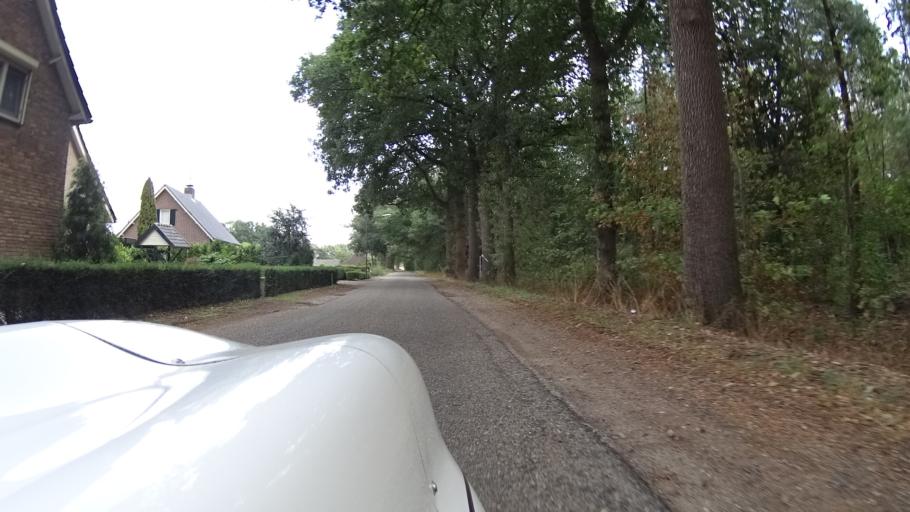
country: NL
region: North Brabant
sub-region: Gemeente Bernheze
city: Loosbroek
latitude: 51.6674
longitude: 5.4966
